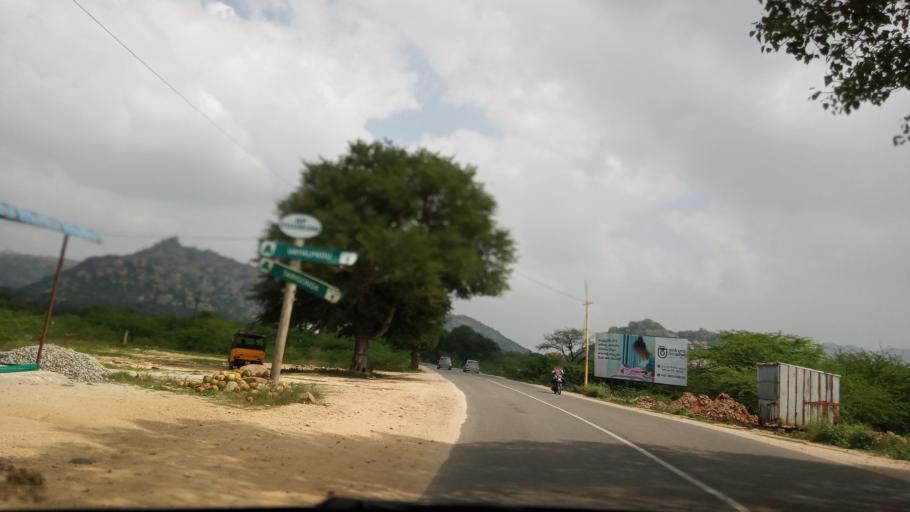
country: IN
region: Andhra Pradesh
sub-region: Chittoor
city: Madanapalle
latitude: 13.6421
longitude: 78.5585
